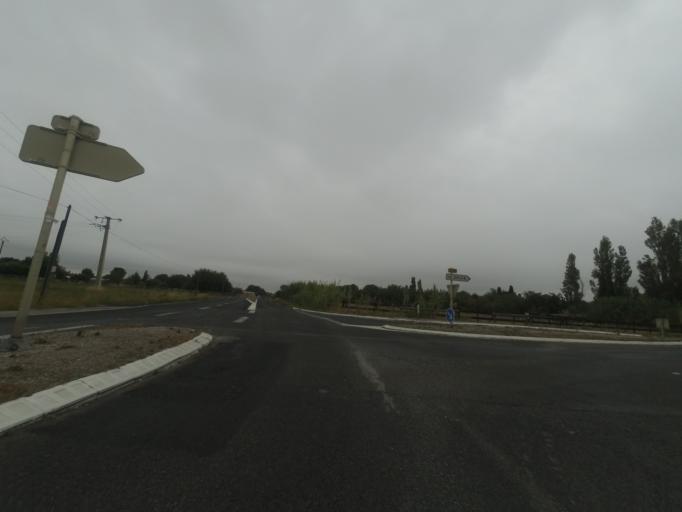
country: FR
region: Languedoc-Roussillon
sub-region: Departement des Pyrenees-Orientales
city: Le Soler
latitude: 42.6928
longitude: 2.7884
